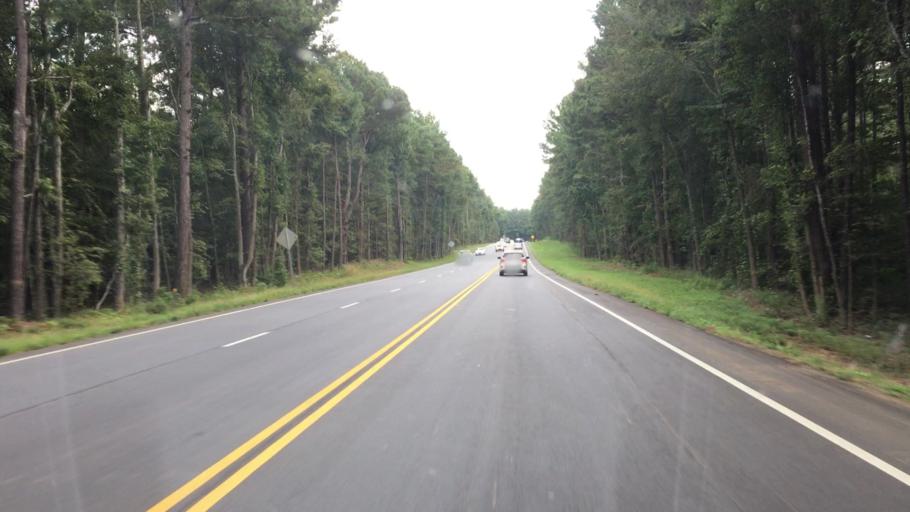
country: US
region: Georgia
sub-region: Putnam County
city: Jefferson
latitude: 33.4371
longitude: -83.3848
